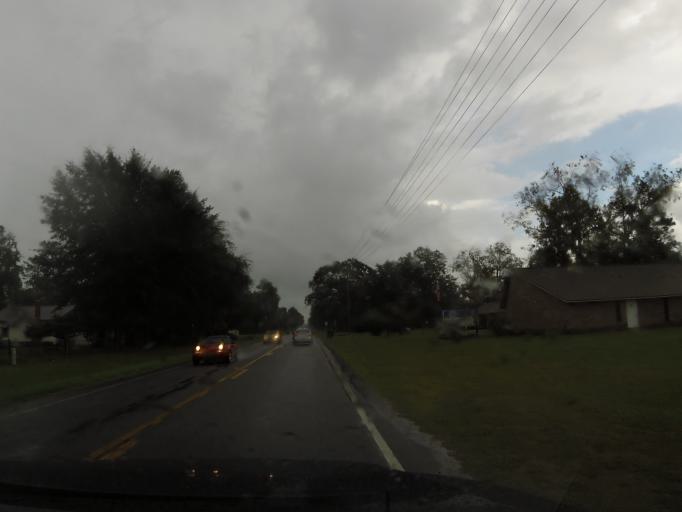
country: US
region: Florida
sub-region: Nassau County
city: Hilliard
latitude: 30.5227
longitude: -82.0353
